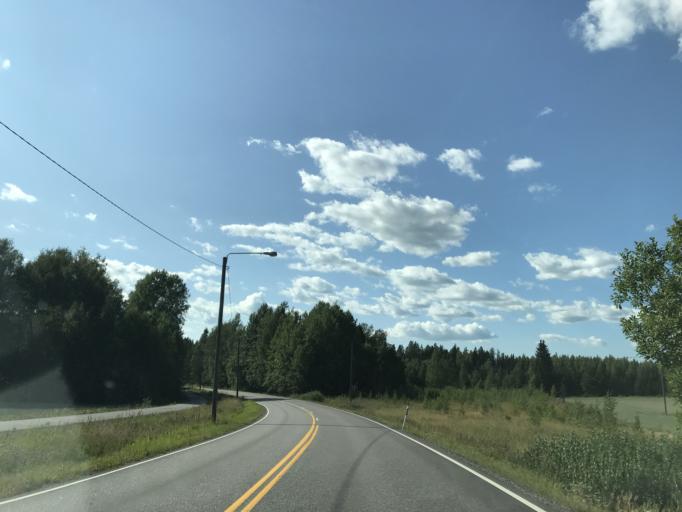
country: FI
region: Uusimaa
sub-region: Helsinki
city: Nurmijaervi
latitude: 60.4091
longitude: 24.8977
